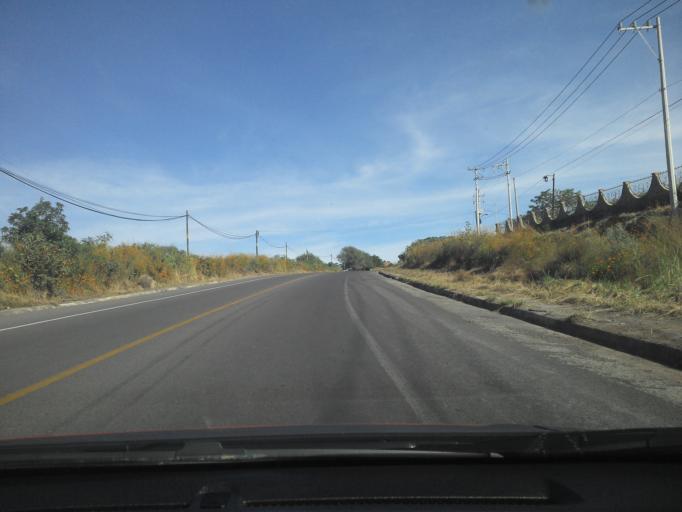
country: MX
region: Jalisco
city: Teuchitlan
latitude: 20.6801
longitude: -103.8419
